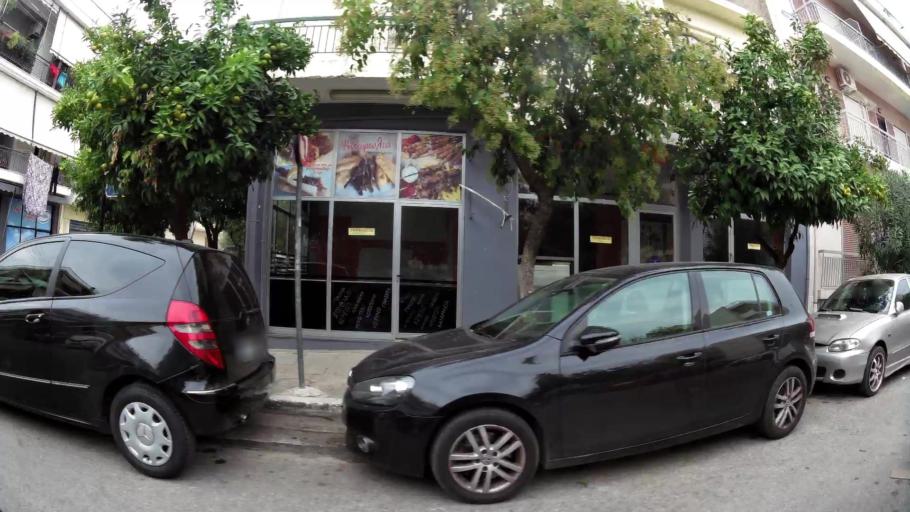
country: GR
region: Attica
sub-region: Nomarchia Athinas
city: Aigaleo
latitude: 37.9901
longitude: 23.6838
